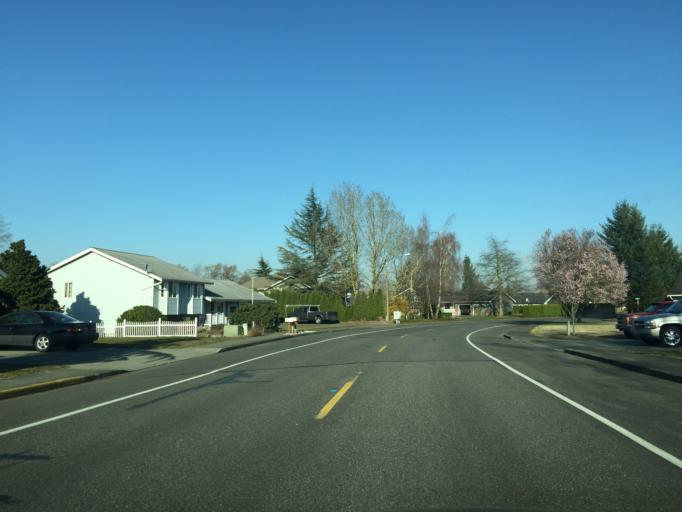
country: US
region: Washington
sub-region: Whatcom County
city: Lynden
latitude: 48.9558
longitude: -122.4375
